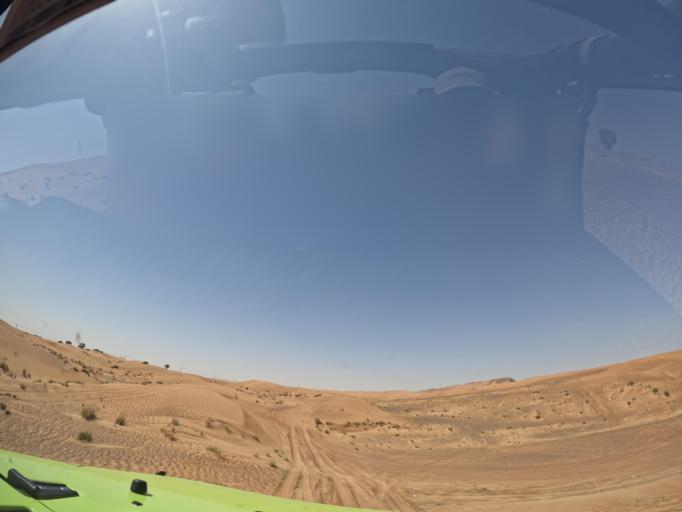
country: AE
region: Ash Shariqah
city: Adh Dhayd
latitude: 25.0195
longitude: 55.7498
